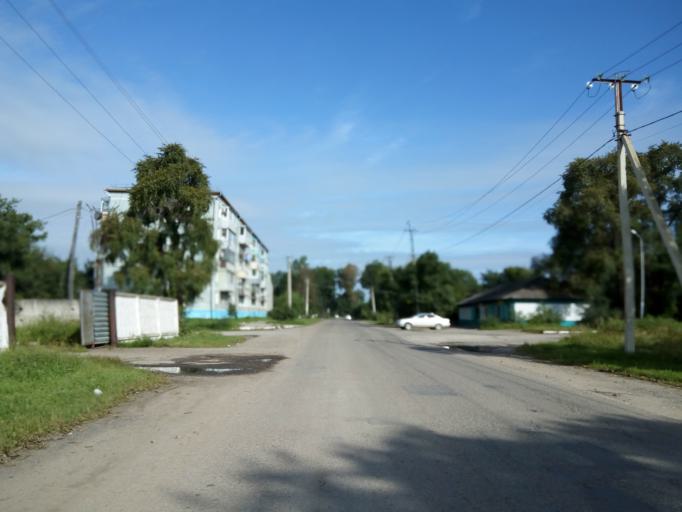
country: RU
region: Primorskiy
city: Dal'nerechensk
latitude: 45.9351
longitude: 133.7448
